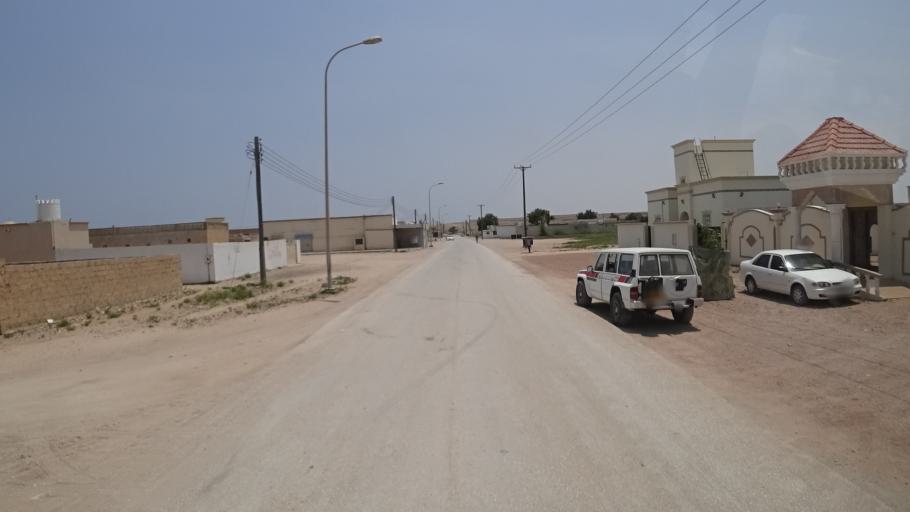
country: OM
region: Ash Sharqiyah
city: Sur
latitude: 22.5121
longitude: 59.7981
